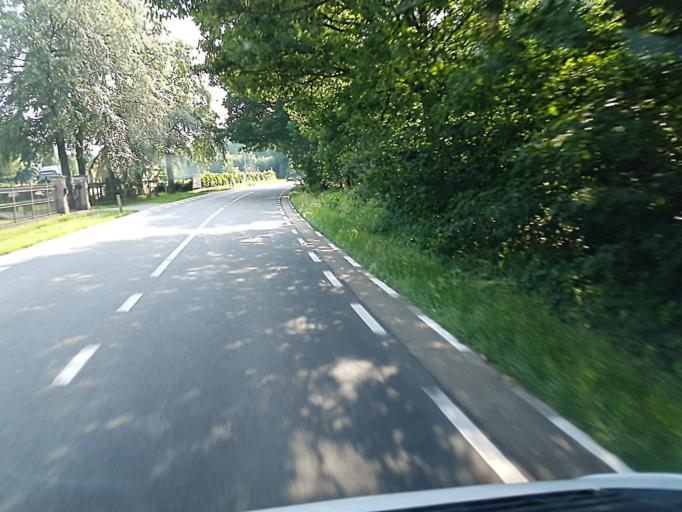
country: BE
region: Flanders
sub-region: Provincie Antwerpen
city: Merksplas
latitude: 51.3758
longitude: 4.8750
